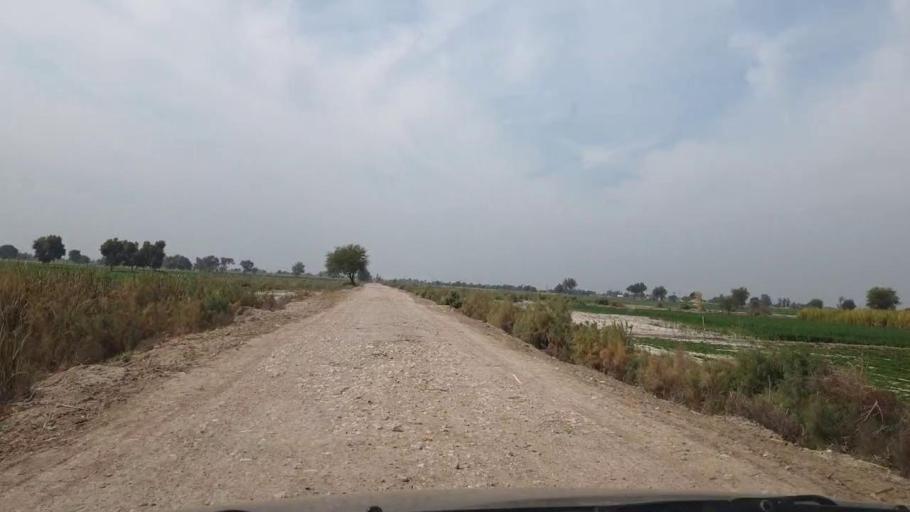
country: PK
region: Sindh
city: Sinjhoro
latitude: 26.0831
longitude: 68.8363
